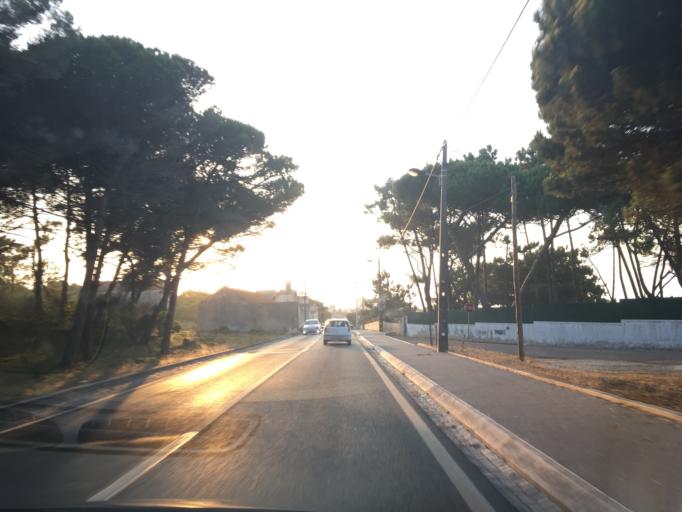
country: PT
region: Lisbon
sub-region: Sintra
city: Colares
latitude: 38.8351
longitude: -9.4564
